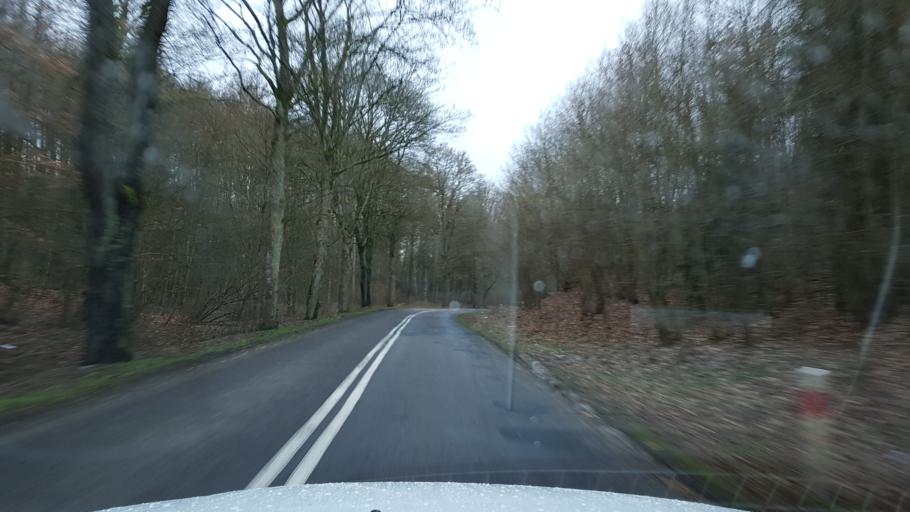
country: PL
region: West Pomeranian Voivodeship
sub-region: Powiat lobeski
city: Lobez
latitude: 53.6533
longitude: 15.5871
